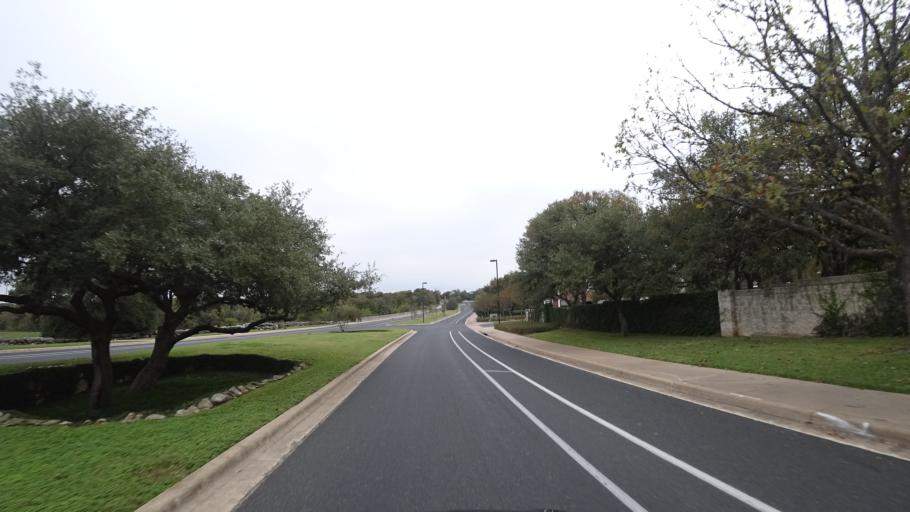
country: US
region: Texas
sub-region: Travis County
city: Shady Hollow
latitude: 30.1849
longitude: -97.8957
